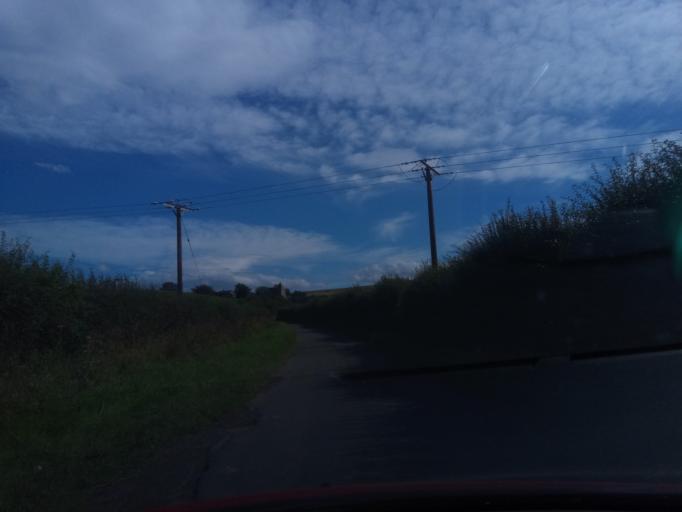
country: GB
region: Scotland
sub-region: The Scottish Borders
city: Coldstream
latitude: 55.6338
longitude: -2.1766
